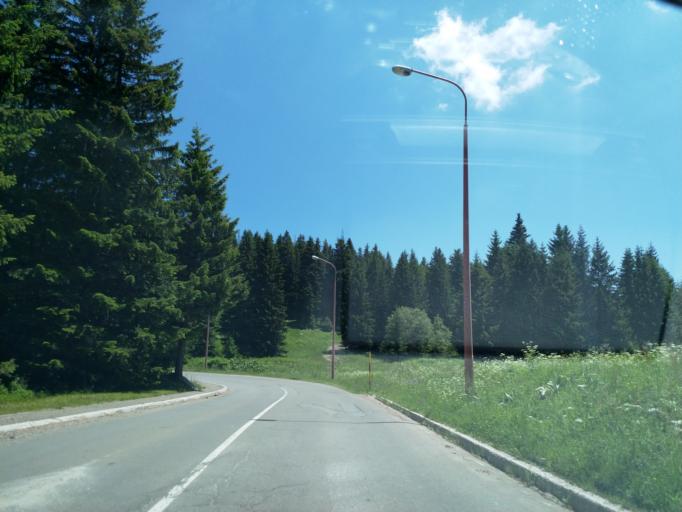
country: XK
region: Mitrovica
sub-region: Komuna e Leposaviqit
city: Leposaviq
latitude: 43.2864
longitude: 20.7985
